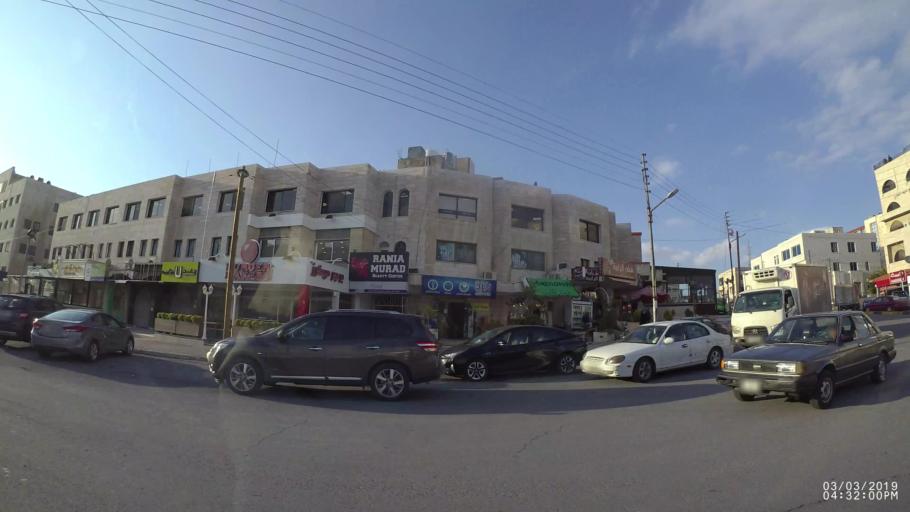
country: JO
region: Amman
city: Al Jubayhah
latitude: 31.9741
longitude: 35.8838
